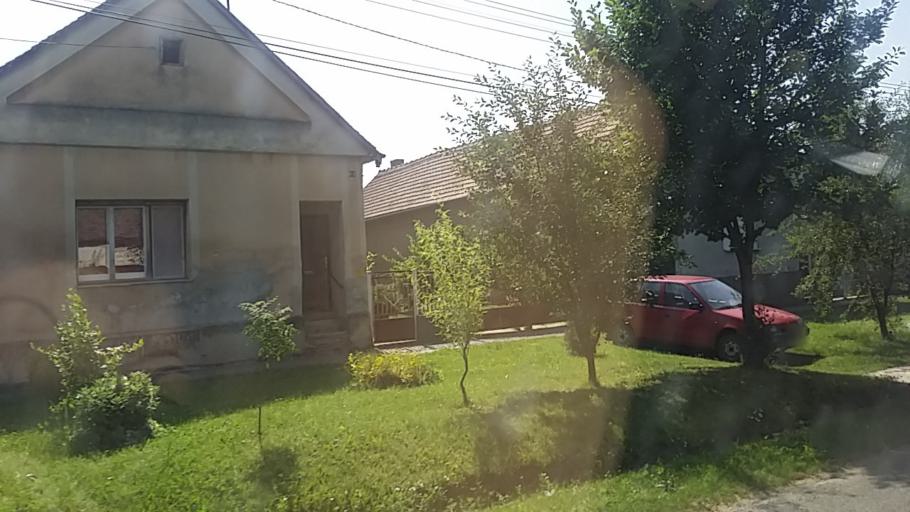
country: HU
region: Baranya
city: Siklos
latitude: 45.9140
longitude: 18.3363
